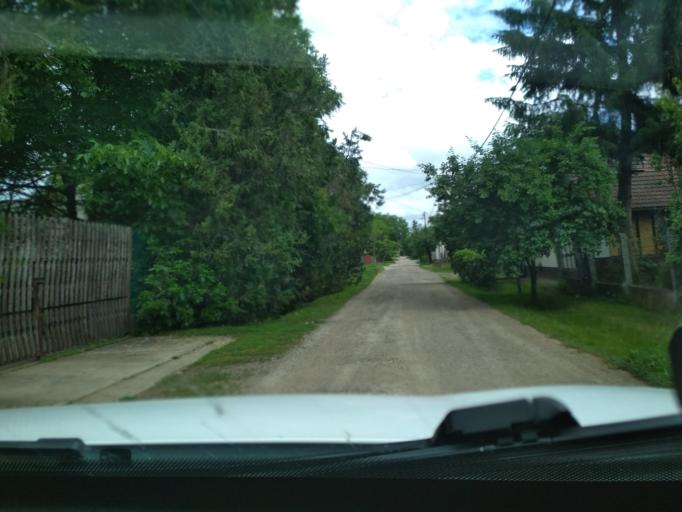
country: HU
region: Jasz-Nagykun-Szolnok
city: Tiszafured
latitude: 47.6092
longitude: 20.7244
